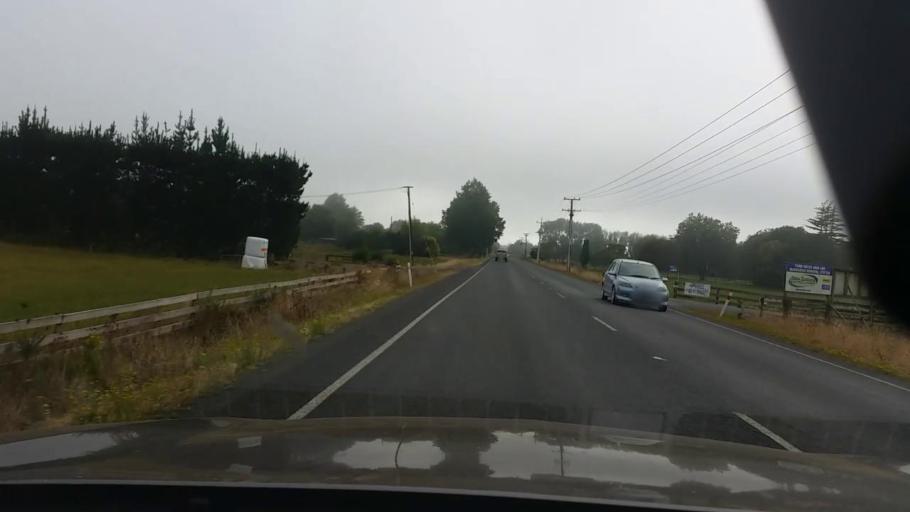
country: NZ
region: Waikato
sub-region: Hamilton City
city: Hamilton
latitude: -37.6282
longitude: 175.3173
